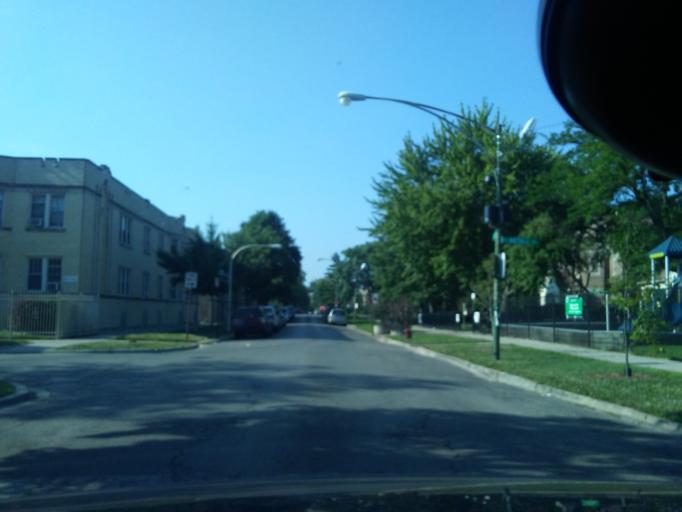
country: US
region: Illinois
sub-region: Cook County
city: Oak Park
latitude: 41.9234
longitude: -87.7512
